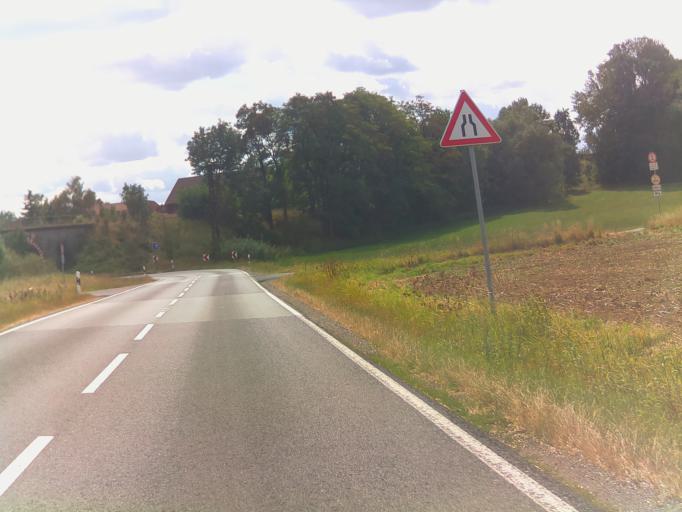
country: DE
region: Thuringia
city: Wolfershausen
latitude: 50.4591
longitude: 10.4390
